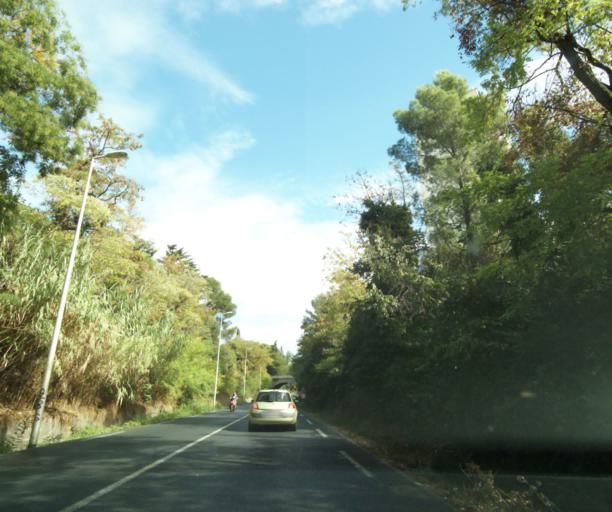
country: FR
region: Languedoc-Roussillon
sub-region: Departement de l'Herault
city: Montpellier
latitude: 43.6090
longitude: 3.8564
